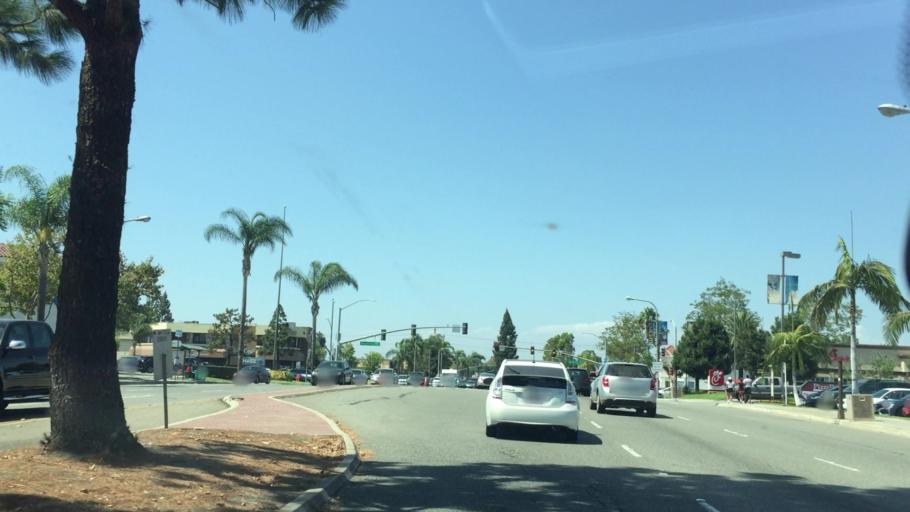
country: US
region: California
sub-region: Orange County
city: Santa Ana
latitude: 33.6988
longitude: -117.8855
